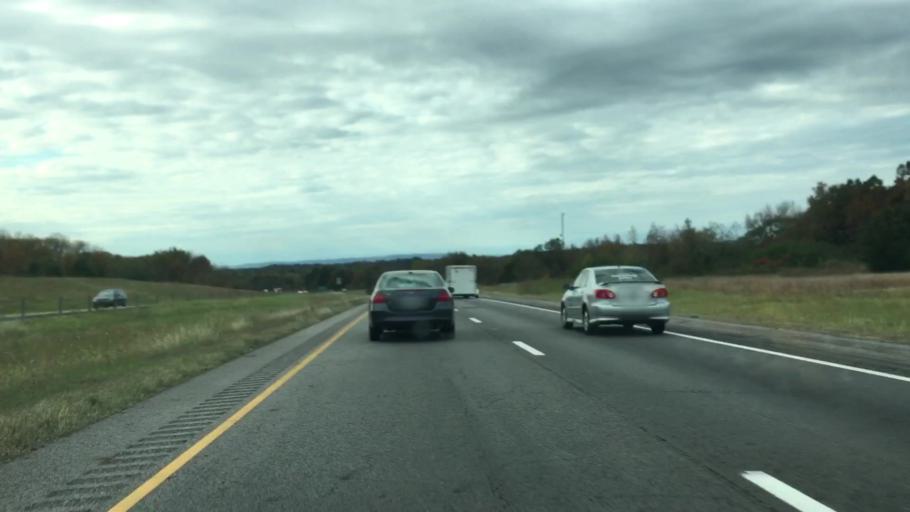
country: US
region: Arkansas
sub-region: Conway County
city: Morrilton
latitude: 35.1718
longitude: -92.6975
